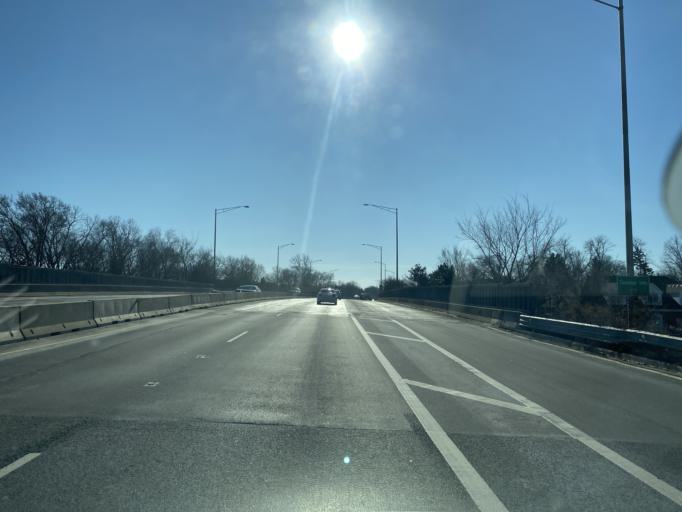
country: US
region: Illinois
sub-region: DuPage County
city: Hinsdale
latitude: 41.8112
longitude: -87.9471
